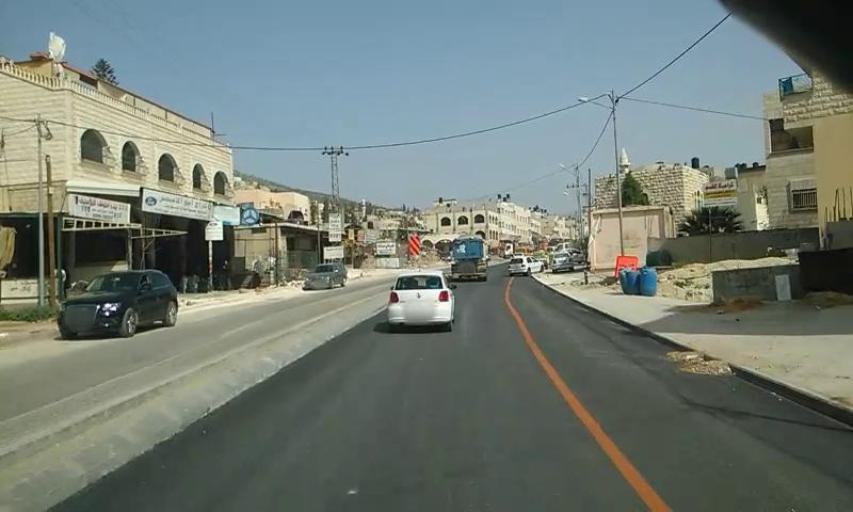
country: PS
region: West Bank
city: Huwwarah
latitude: 32.1479
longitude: 35.2578
